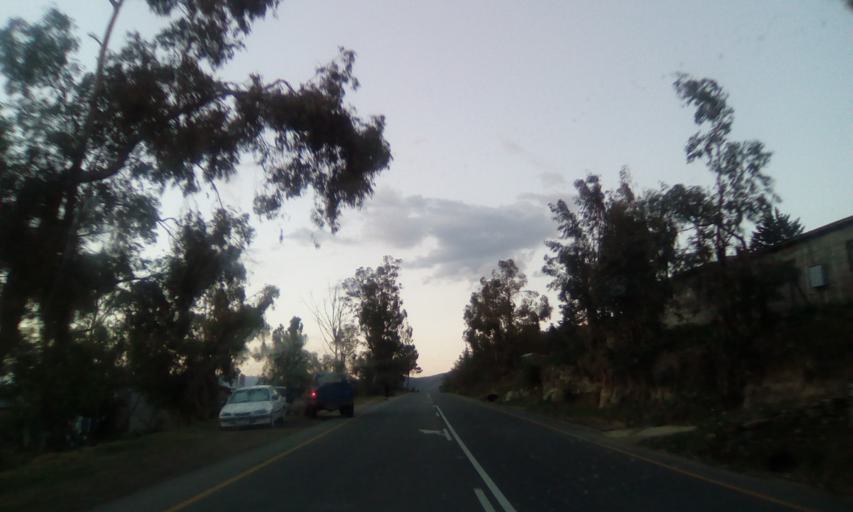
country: LS
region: Qacha's Nek
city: Qacha's Nek
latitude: -30.1262
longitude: 28.6885
